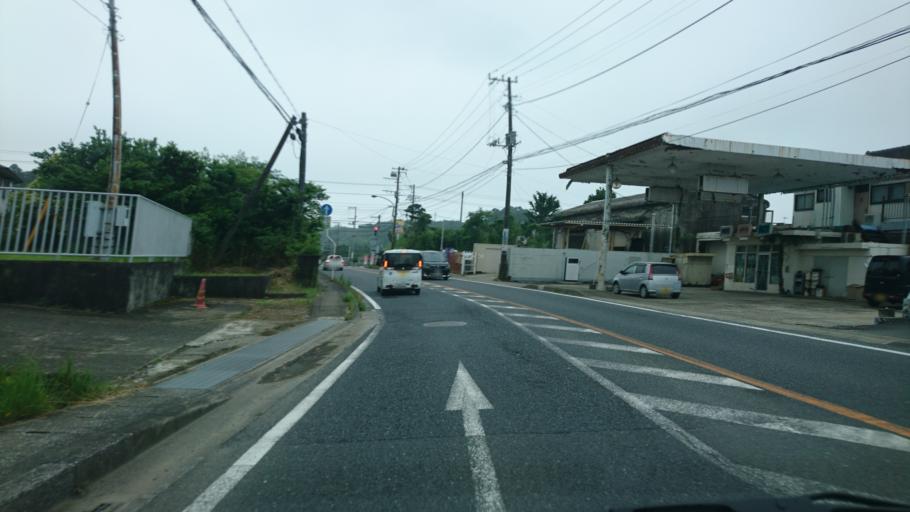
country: JP
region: Chiba
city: Kimitsu
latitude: 35.2628
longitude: 139.8853
